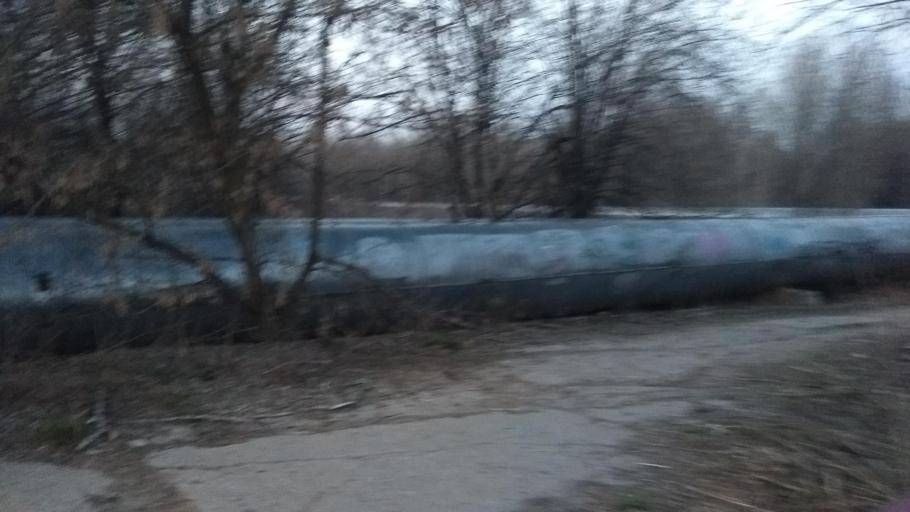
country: RU
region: Moscow
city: Biryulevo
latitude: 55.5867
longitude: 37.6996
